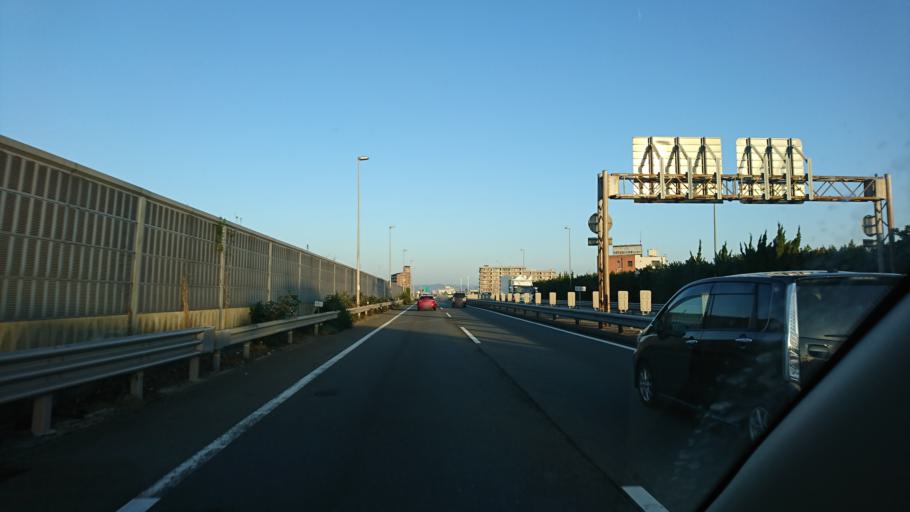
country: JP
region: Hyogo
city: Kakogawacho-honmachi
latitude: 34.7217
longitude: 134.8969
